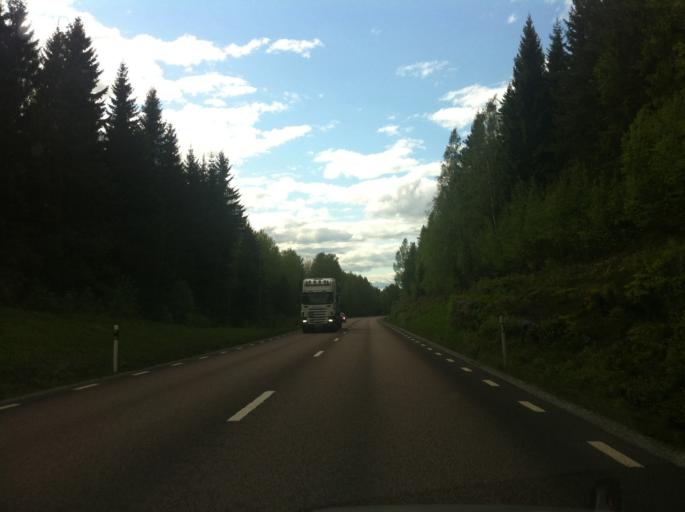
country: SE
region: Vaermland
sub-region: Filipstads Kommun
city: Filipstad
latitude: 59.6553
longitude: 14.2278
